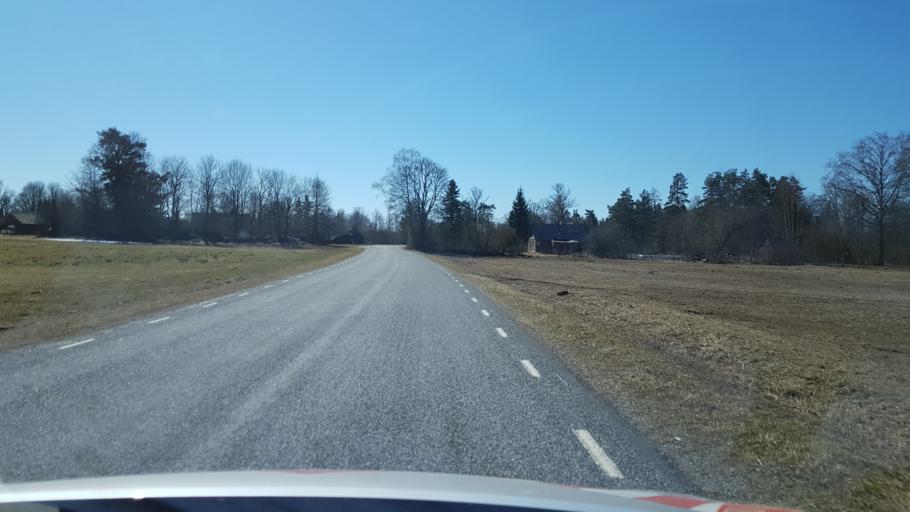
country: EE
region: Laeaene-Virumaa
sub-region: Haljala vald
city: Haljala
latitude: 59.4685
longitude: 26.2423
